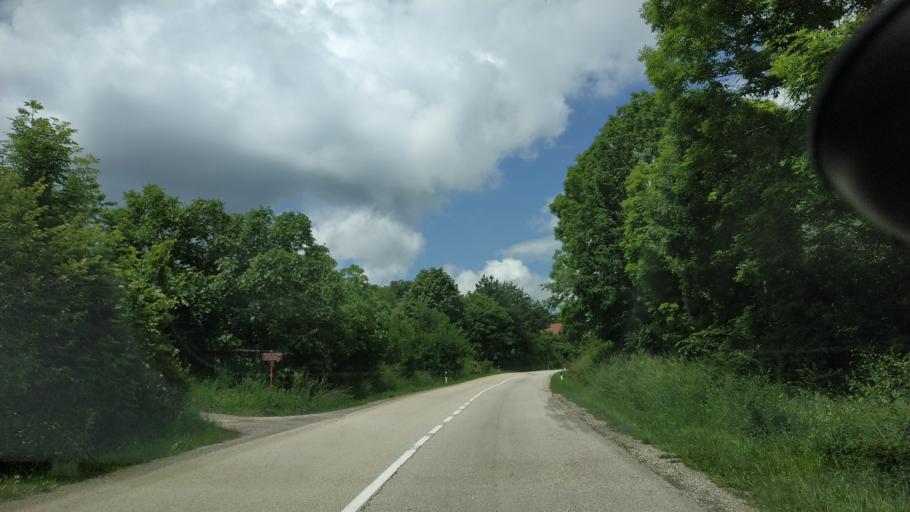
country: RS
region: Central Serbia
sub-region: Borski Okrug
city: Bor
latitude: 44.0835
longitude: 22.0104
